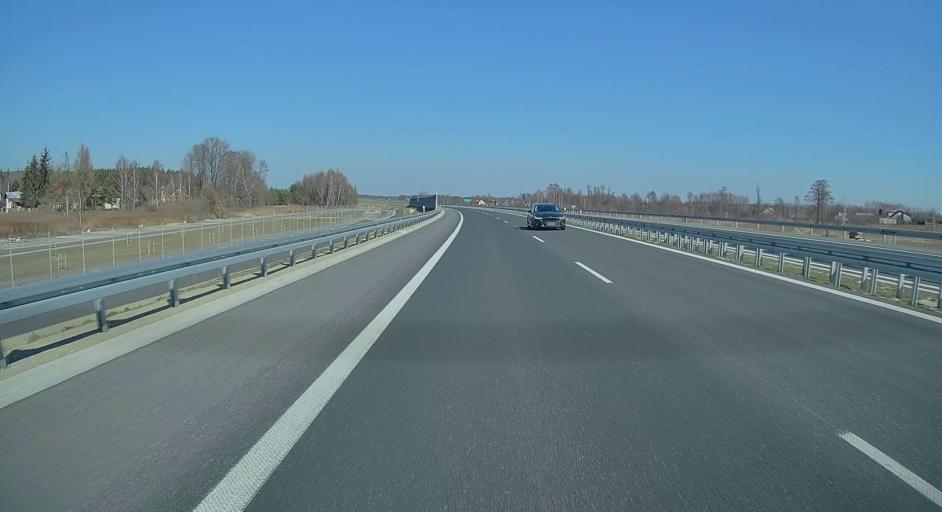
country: PL
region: Subcarpathian Voivodeship
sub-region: Powiat lezajski
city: Letownia
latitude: 50.3385
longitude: 22.2003
